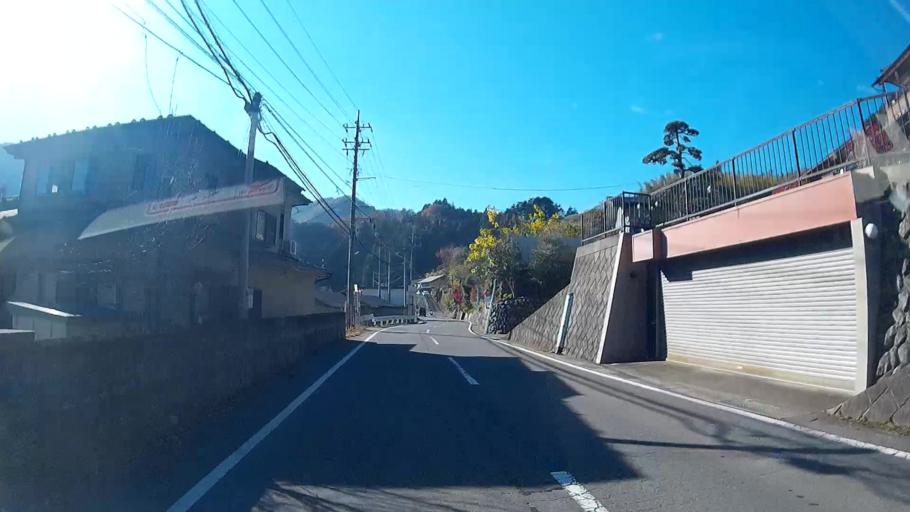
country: JP
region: Yamanashi
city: Uenohara
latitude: 35.5799
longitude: 139.1034
